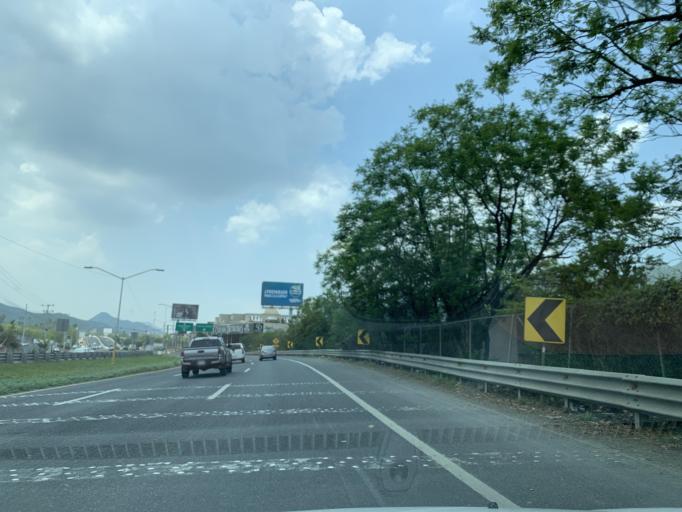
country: MX
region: Nuevo Leon
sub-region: Juarez
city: Bosques de San Pedro
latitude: 25.5189
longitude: -100.2012
